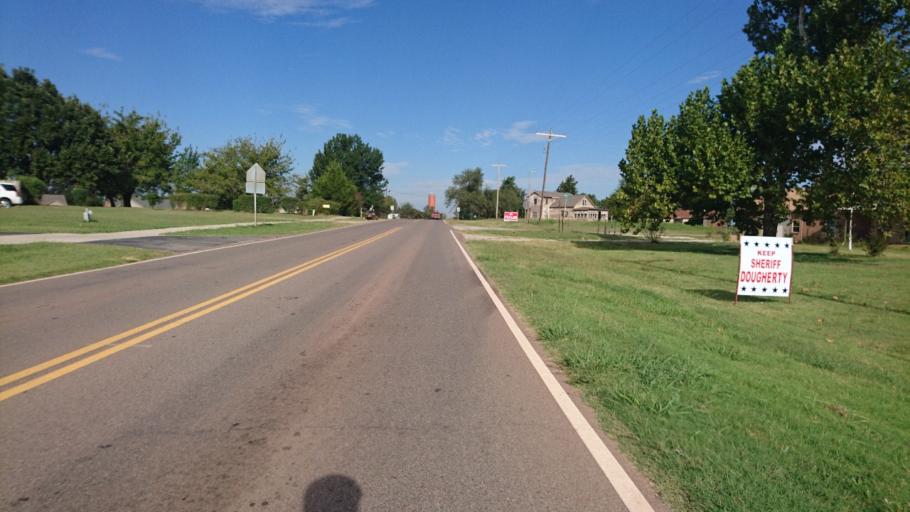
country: US
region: Oklahoma
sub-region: Oklahoma County
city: Luther
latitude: 35.6856
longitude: -97.0601
